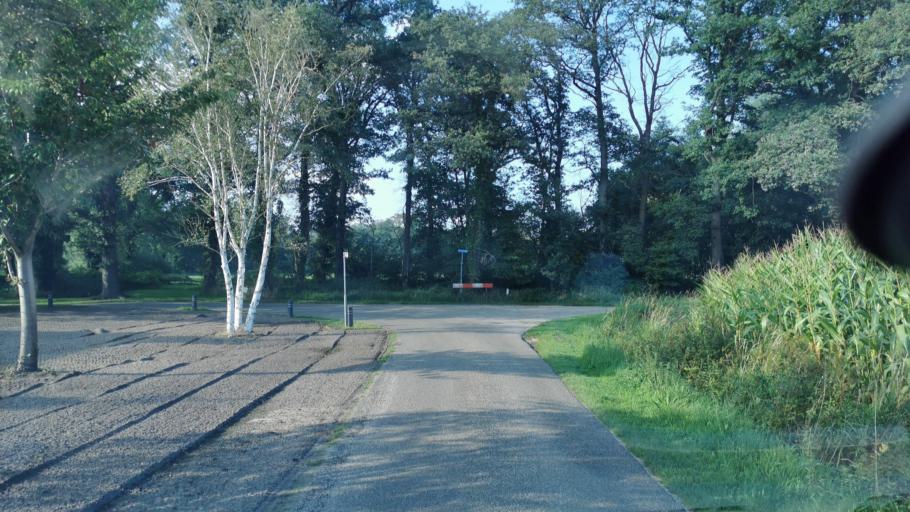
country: NL
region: Overijssel
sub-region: Gemeente Tubbergen
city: Tubbergen
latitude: 52.3581
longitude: 6.8145
